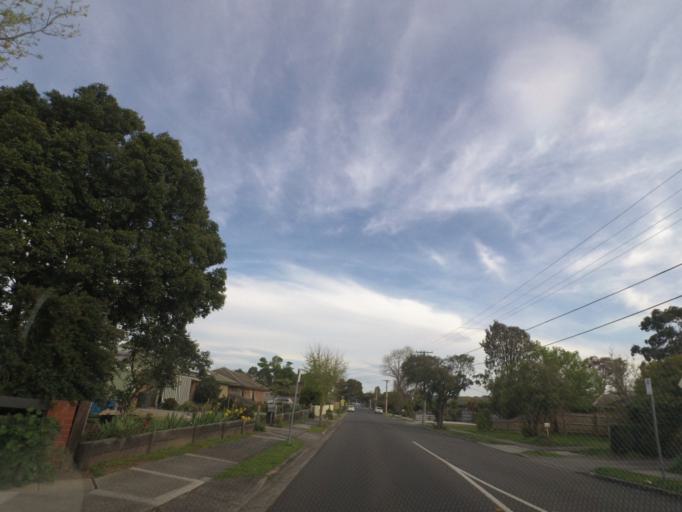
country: AU
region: Victoria
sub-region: Knox
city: Scoresby
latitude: -37.8941
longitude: 145.2405
